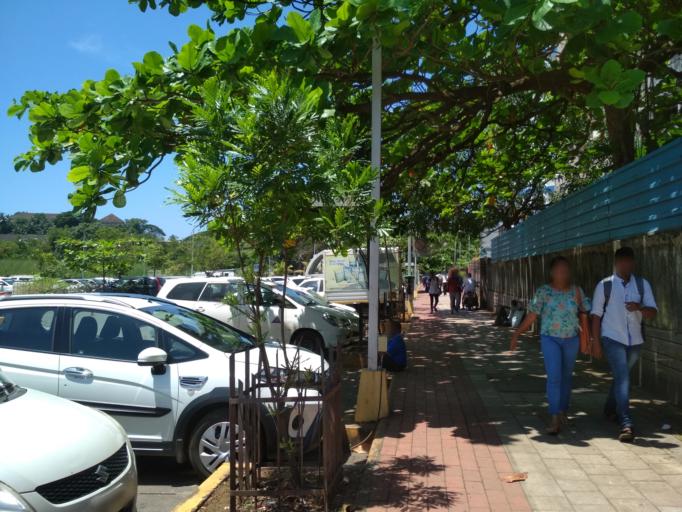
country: IN
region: Goa
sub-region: North Goa
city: Panaji
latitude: 15.4963
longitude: 73.8341
